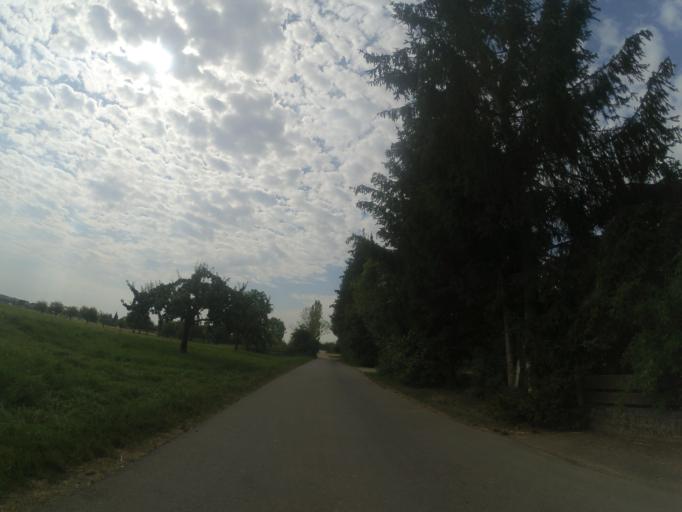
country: DE
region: Baden-Wuerttemberg
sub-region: Tuebingen Region
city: Dornstadt
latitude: 48.4881
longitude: 9.9016
